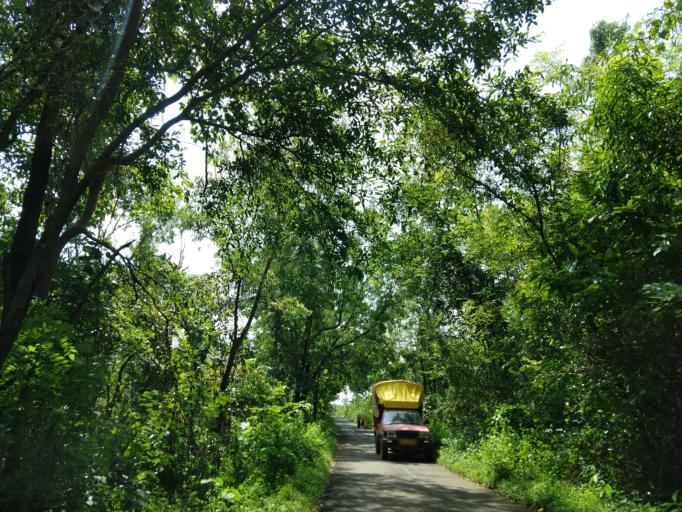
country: IN
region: Maharashtra
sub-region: Sindhudurg
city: Kudal
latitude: 16.0489
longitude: 73.6805
